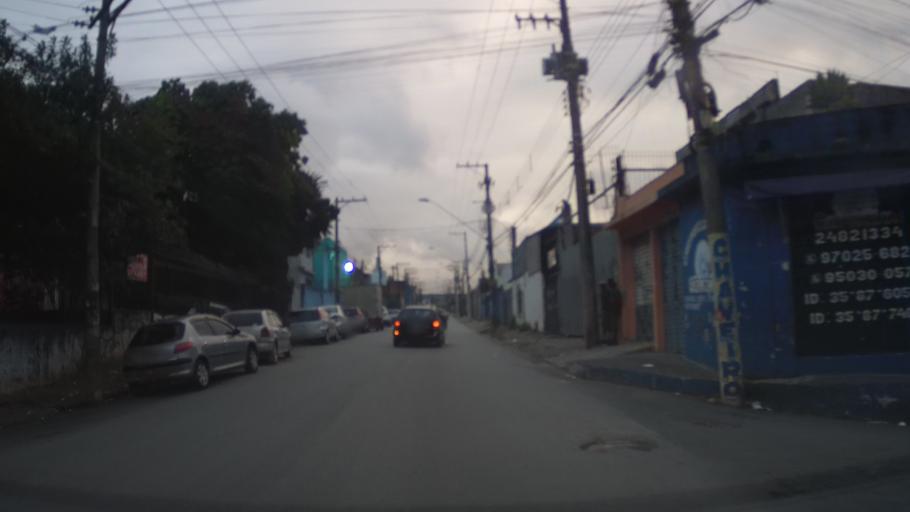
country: BR
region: Sao Paulo
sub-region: Guarulhos
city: Guarulhos
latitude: -23.4575
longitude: -46.4635
